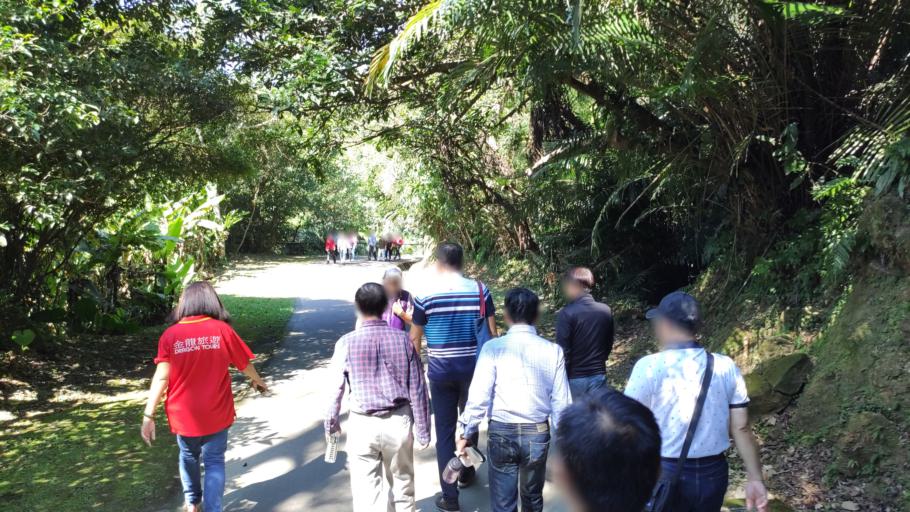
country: TW
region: Taiwan
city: Daxi
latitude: 24.8408
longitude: 121.3071
